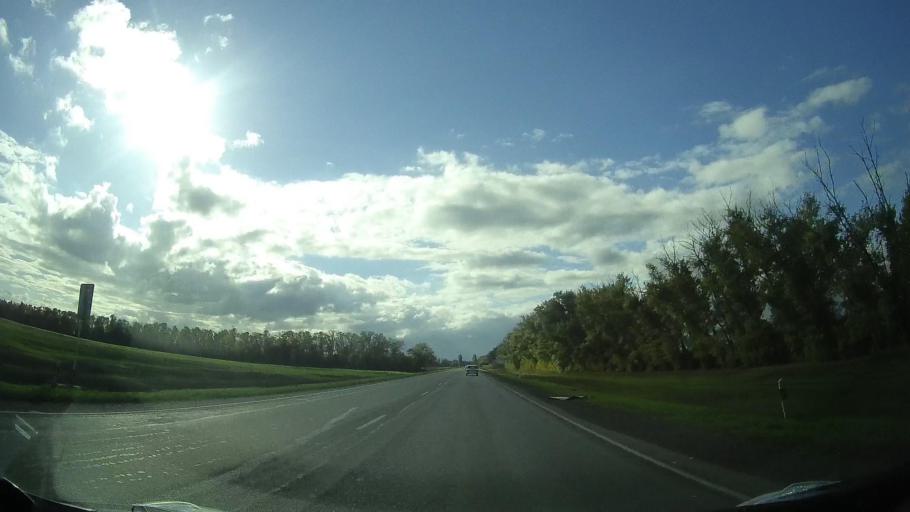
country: RU
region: Rostov
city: Tselina
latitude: 46.5317
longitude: 40.9666
